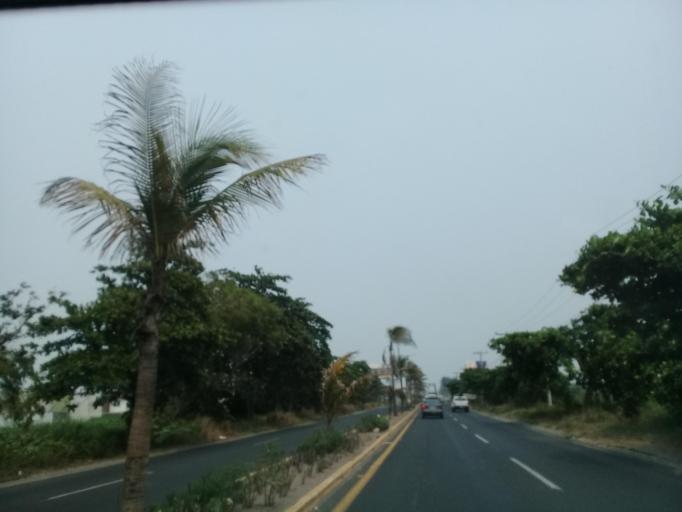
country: MX
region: Veracruz
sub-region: Veracruz
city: Hacienda Sotavento
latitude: 19.1454
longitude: -96.1632
